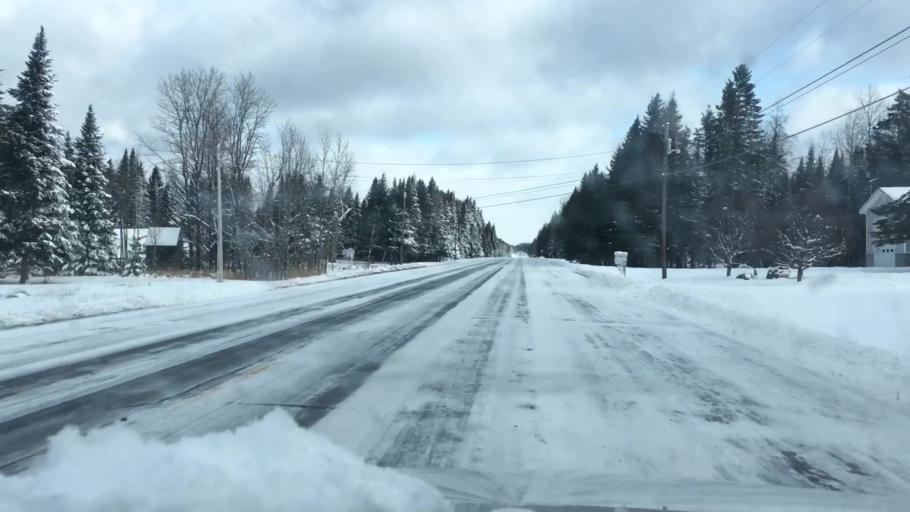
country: US
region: Maine
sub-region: Aroostook County
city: Madawaska
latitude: 47.0130
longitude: -68.0184
